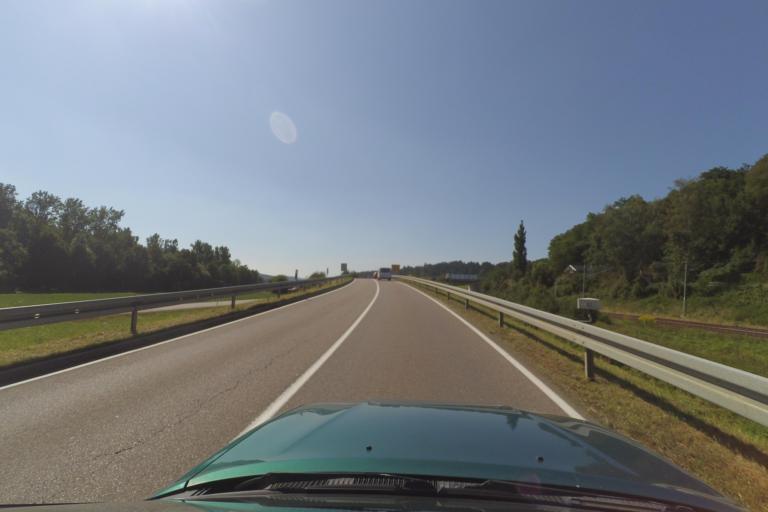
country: DE
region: Baden-Wuerttemberg
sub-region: Regierungsbezirk Stuttgart
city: Iggingen
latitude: 48.8234
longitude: 9.8930
